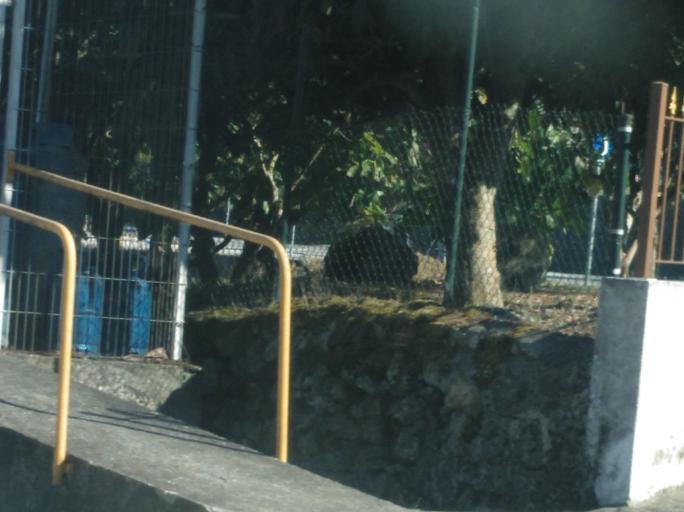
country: PT
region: Leiria
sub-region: Porto de Mos
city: Porto de Mos
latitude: 39.5860
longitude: -8.8103
